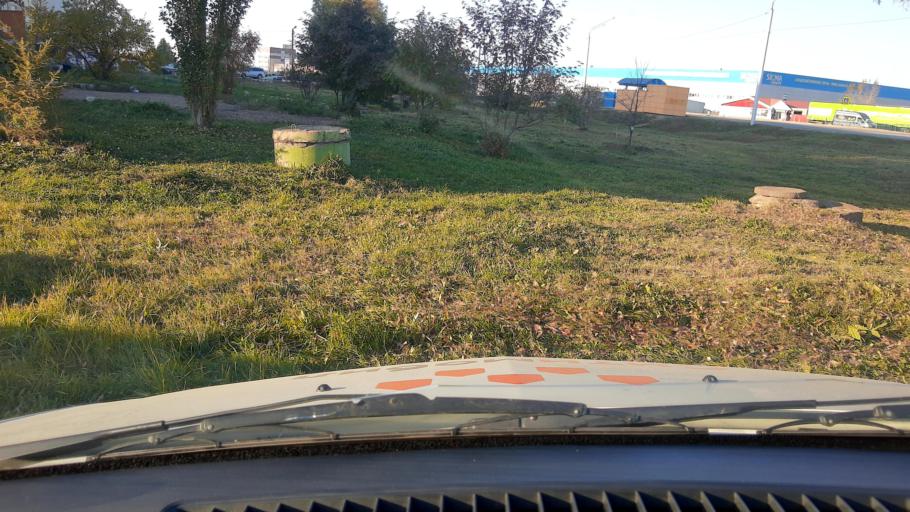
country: RU
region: Bashkortostan
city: Iglino
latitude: 54.7551
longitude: 56.2488
